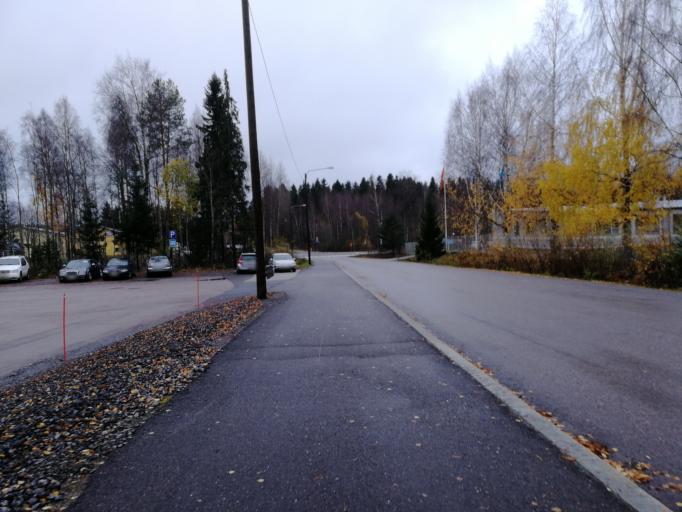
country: FI
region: Pirkanmaa
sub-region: Tampere
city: Tampere
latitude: 61.4543
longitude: 23.8839
